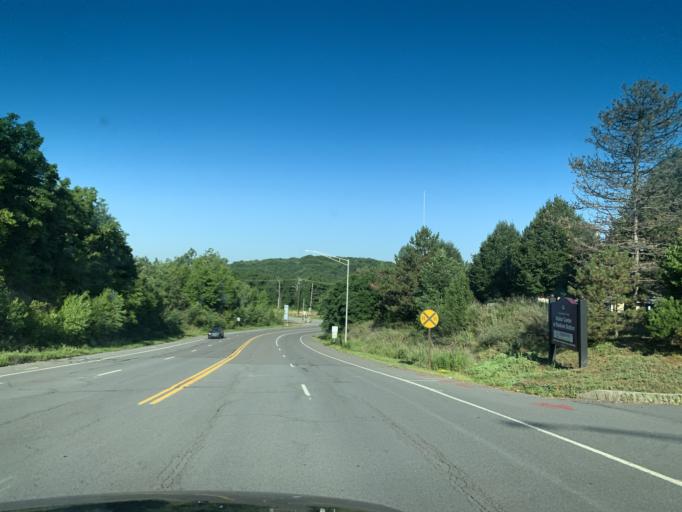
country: US
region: Pennsylvania
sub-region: Lackawanna County
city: Taylor
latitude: 41.3651
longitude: -75.6848
